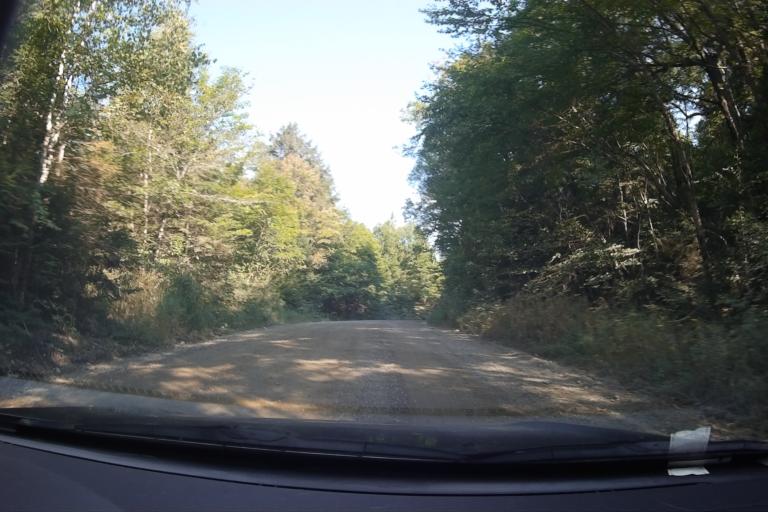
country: CA
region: Ontario
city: Huntsville
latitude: 45.5462
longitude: -78.6952
